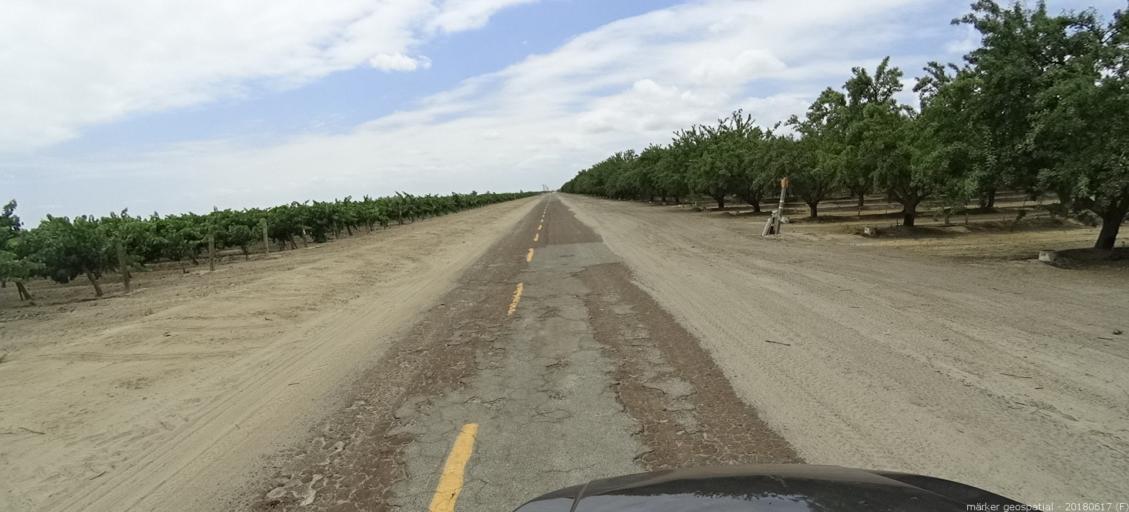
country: US
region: California
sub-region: Fresno County
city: Kerman
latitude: 36.8198
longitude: -120.1690
